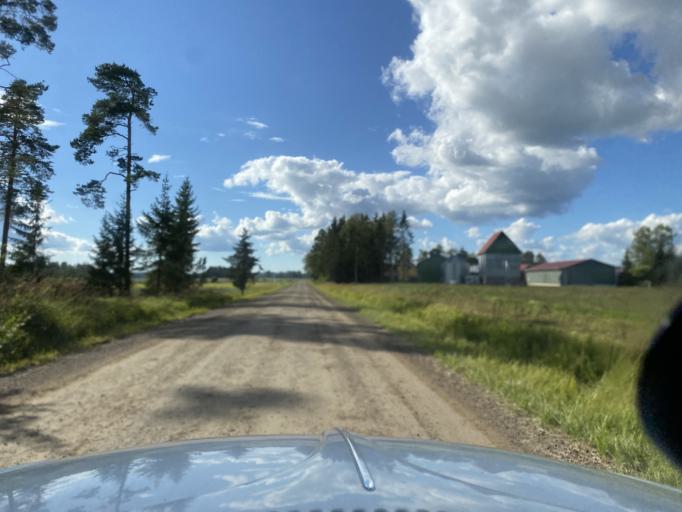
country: FI
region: Pirkanmaa
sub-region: Lounais-Pirkanmaa
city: Punkalaidun
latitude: 61.1284
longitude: 23.2484
